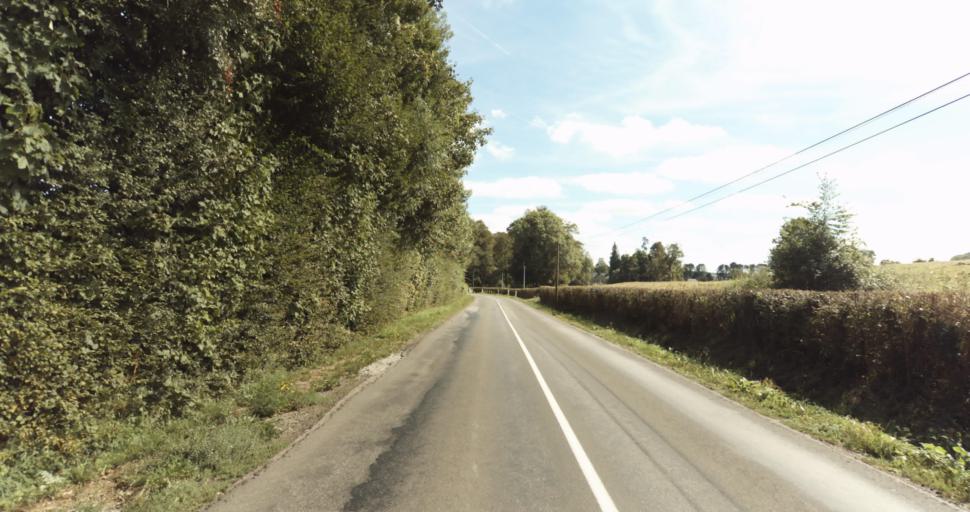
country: FR
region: Lower Normandy
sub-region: Departement de l'Orne
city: Vimoutiers
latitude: 48.9065
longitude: 0.2658
